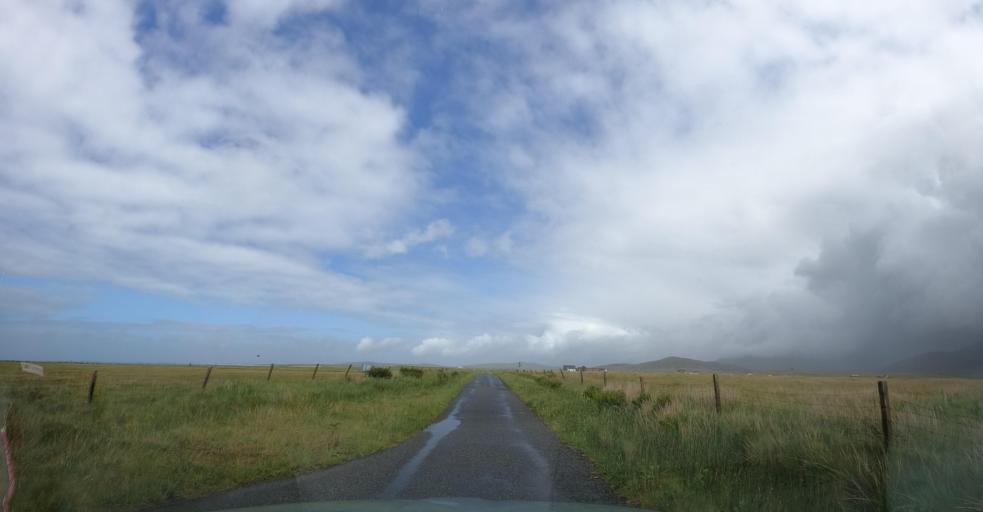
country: GB
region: Scotland
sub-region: Eilean Siar
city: Isle of South Uist
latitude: 57.2884
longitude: -7.4118
